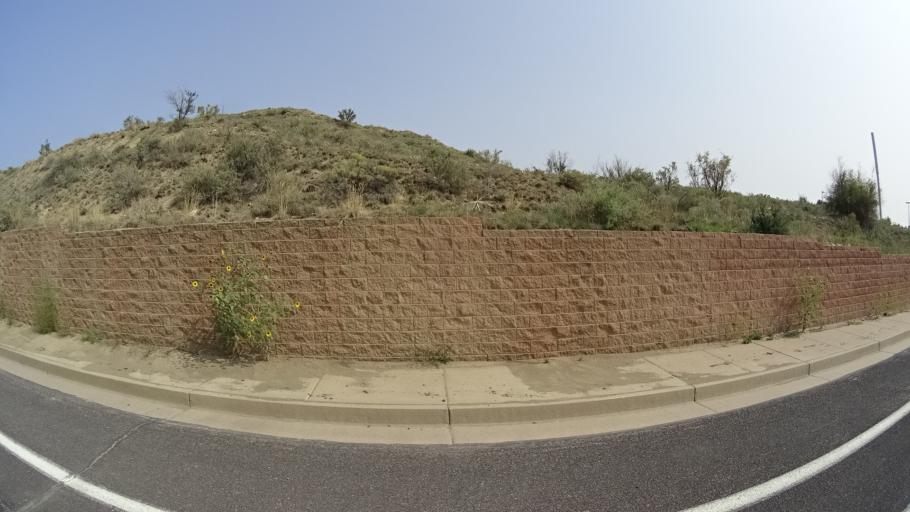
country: US
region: Colorado
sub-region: El Paso County
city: Colorado Springs
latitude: 38.8126
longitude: -104.8016
